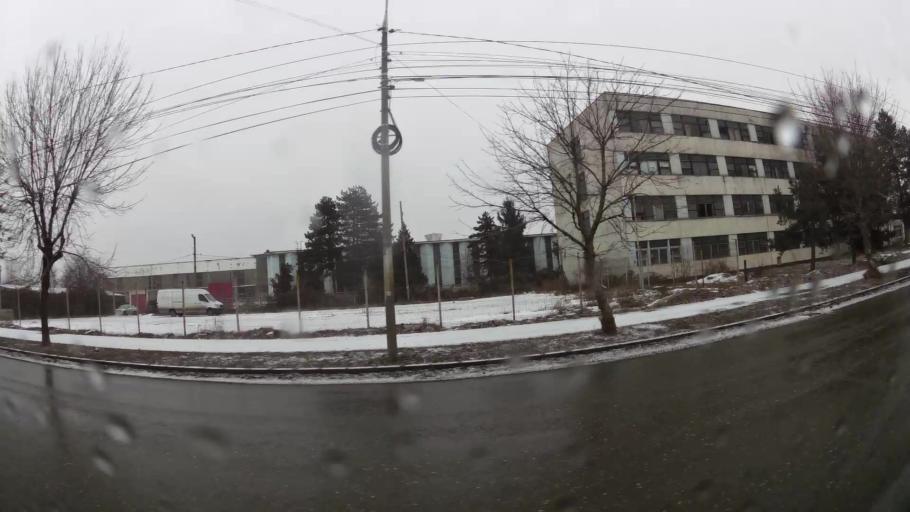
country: RO
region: Dambovita
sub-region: Municipiul Targoviste
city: Targoviste
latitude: 44.9168
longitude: 25.4396
